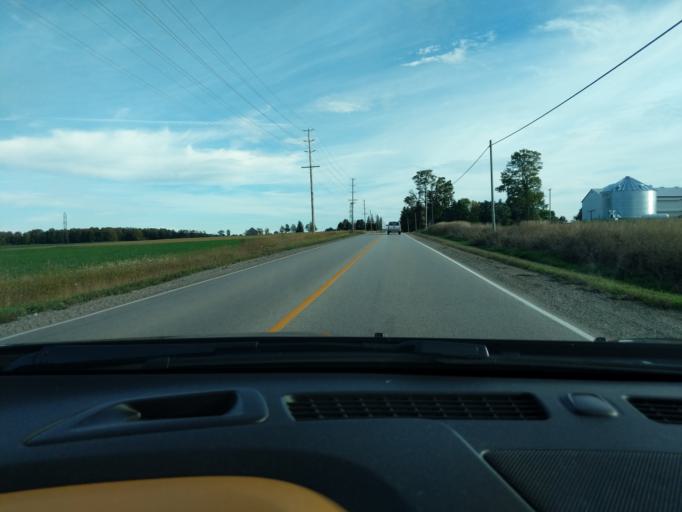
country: CA
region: Ontario
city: Barrie
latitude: 44.4140
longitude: -79.7531
